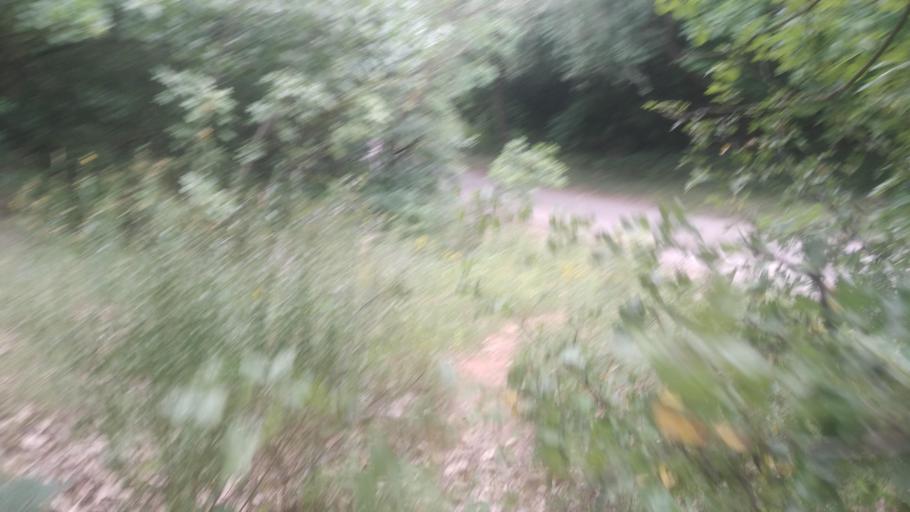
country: HU
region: Veszprem
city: Szentkiralyszabadja
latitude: 46.9992
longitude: 17.9737
